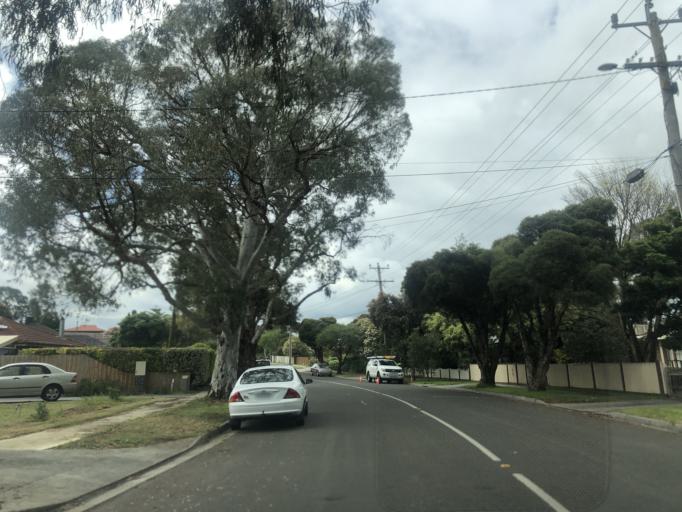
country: AU
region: Victoria
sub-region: Knox
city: Rowville
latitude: -37.9383
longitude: 145.2249
